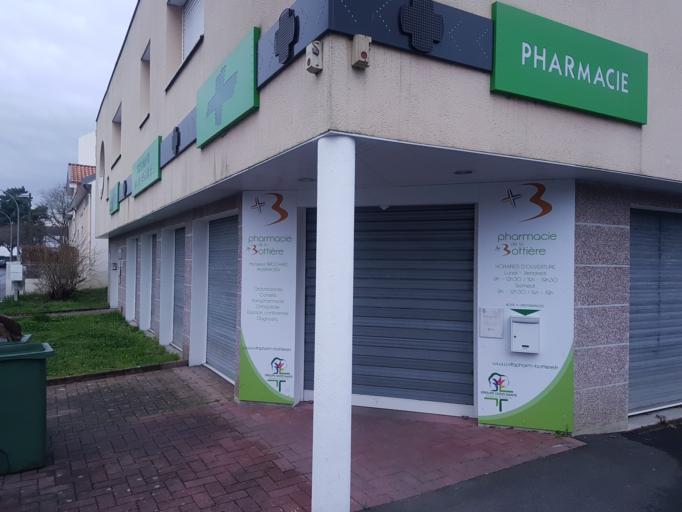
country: FR
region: Pays de la Loire
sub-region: Departement de la Loire-Atlantique
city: Saint-Sebastien-sur-Loire
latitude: 47.2396
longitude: -1.5194
